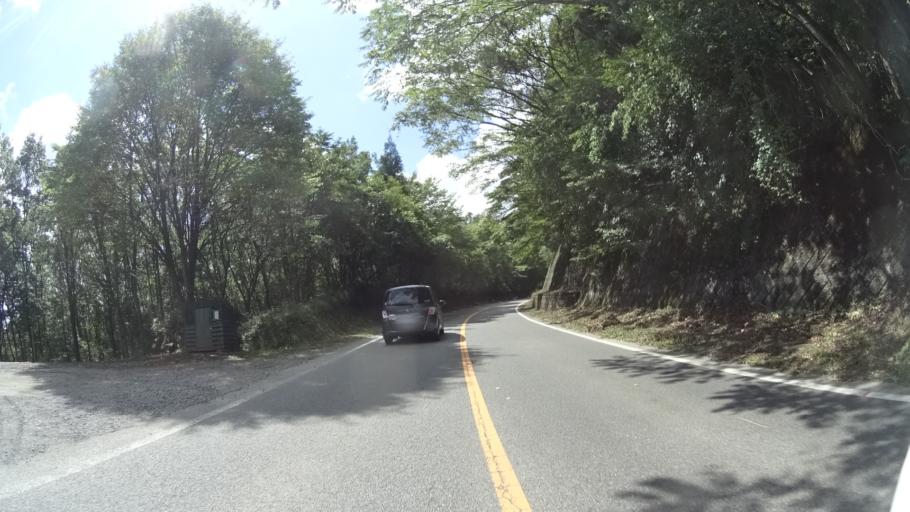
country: JP
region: Oita
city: Tsukawaki
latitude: 33.2248
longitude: 131.2995
